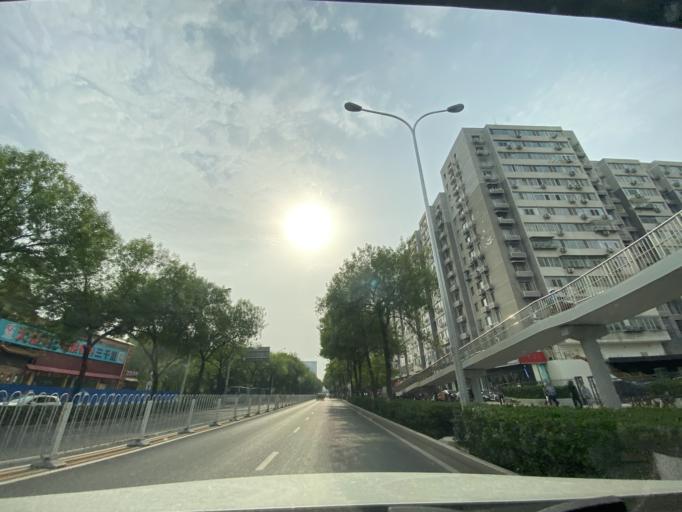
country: CN
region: Beijing
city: Qinghe
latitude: 39.9753
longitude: 116.3546
